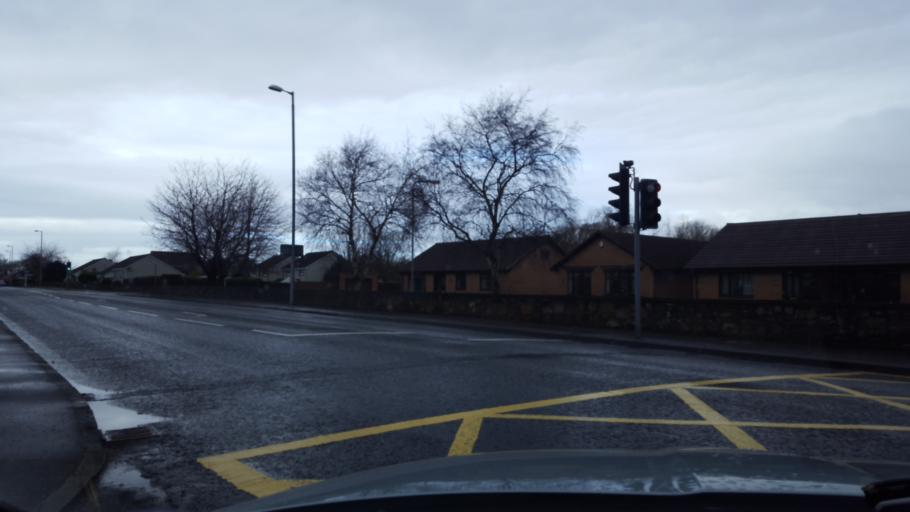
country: GB
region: Scotland
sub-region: South Ayrshire
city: Prestwick
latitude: 55.4553
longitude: -4.5989
